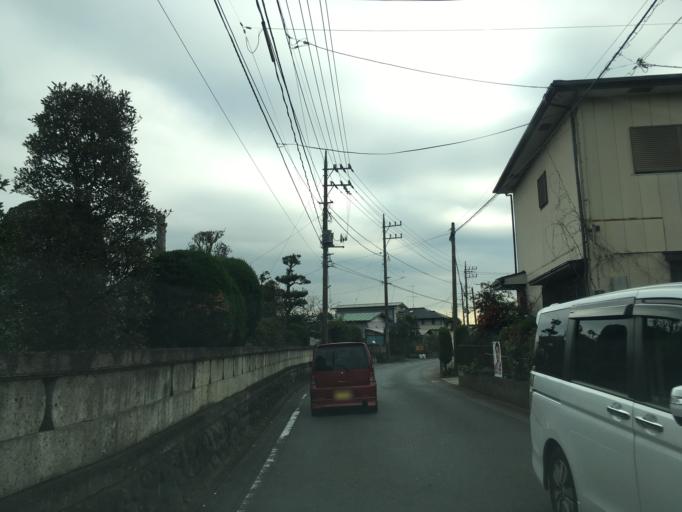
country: JP
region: Tokyo
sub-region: Machida-shi
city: Machida
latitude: 35.5165
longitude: 139.4633
